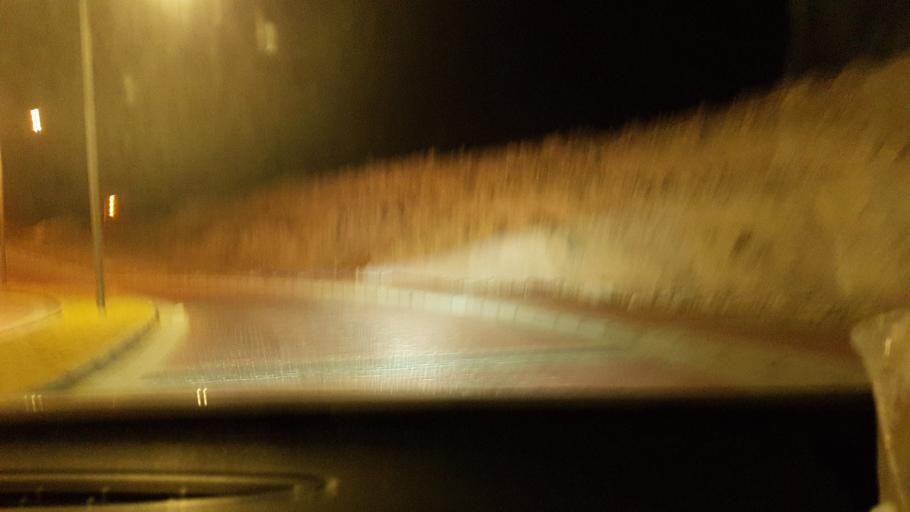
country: EG
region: Muhafazat Matruh
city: Al `Alamayn
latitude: 31.0634
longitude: 28.3621
